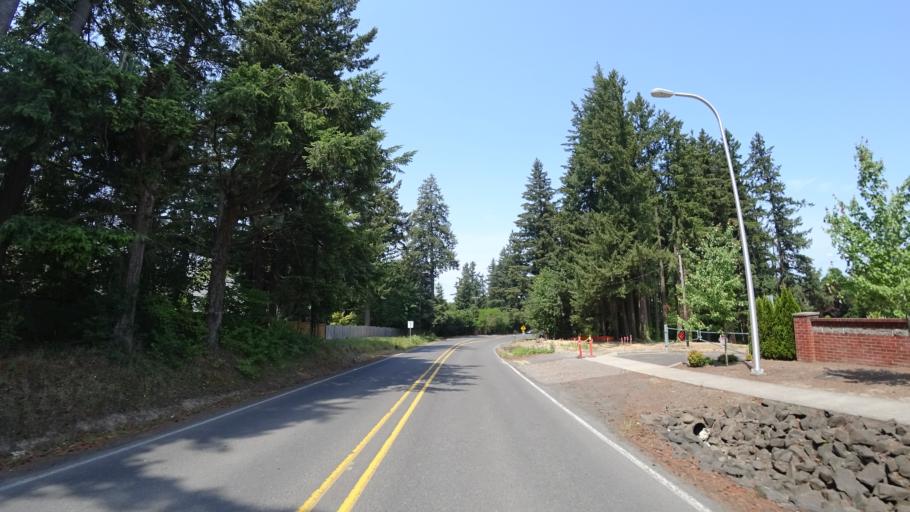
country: US
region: Oregon
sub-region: Washington County
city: Oak Hills
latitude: 45.5435
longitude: -122.8364
